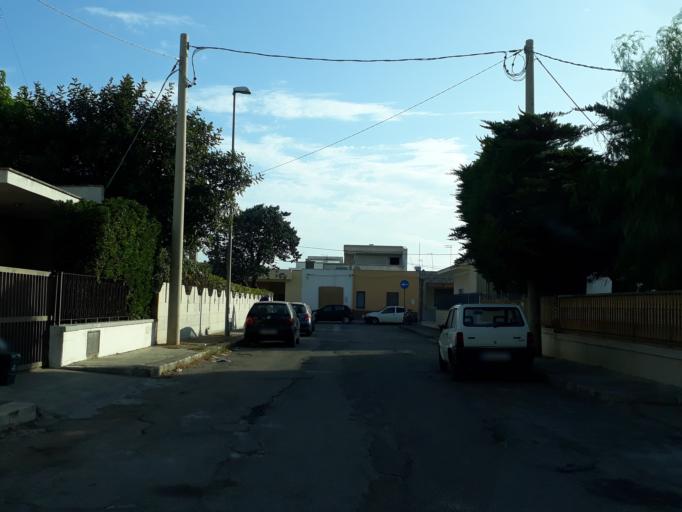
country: IT
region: Apulia
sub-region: Provincia di Brindisi
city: Carovigno
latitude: 40.7564
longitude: 17.7007
